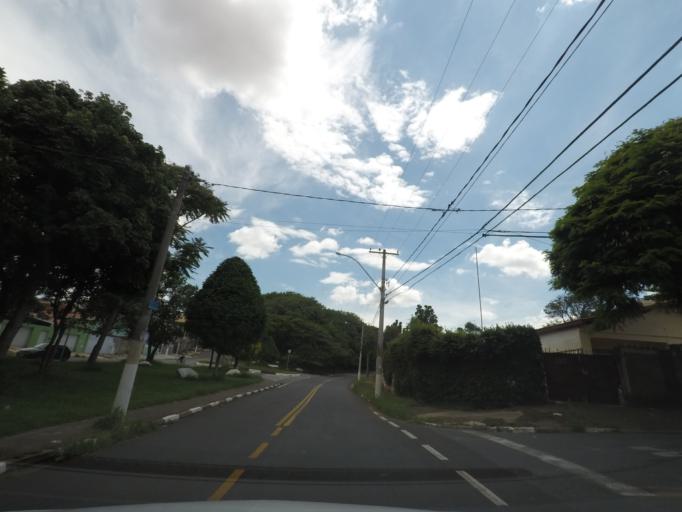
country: BR
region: Sao Paulo
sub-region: Campinas
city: Campinas
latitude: -22.9190
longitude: -47.0365
